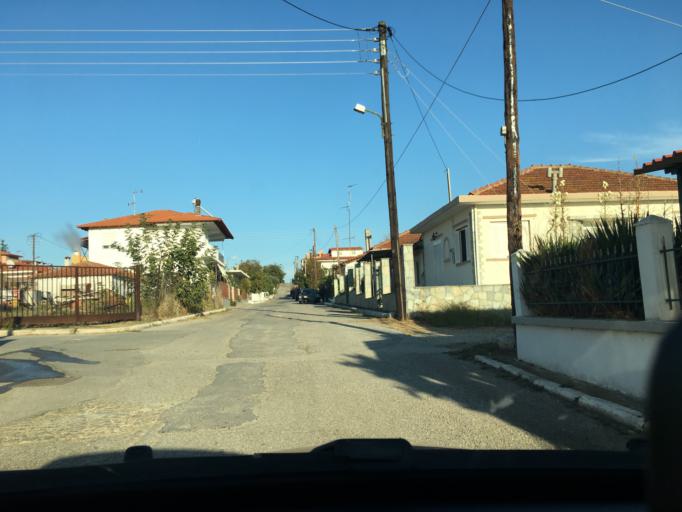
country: GR
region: Central Macedonia
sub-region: Nomos Chalkidikis
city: Nea Poteidaia
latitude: 40.1923
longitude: 23.3284
